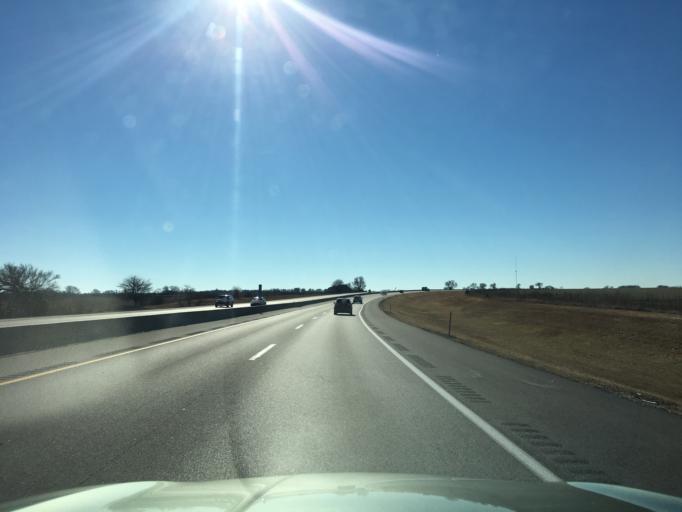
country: US
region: Kansas
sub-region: Sumner County
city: Belle Plaine
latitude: 37.3483
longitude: -97.3220
